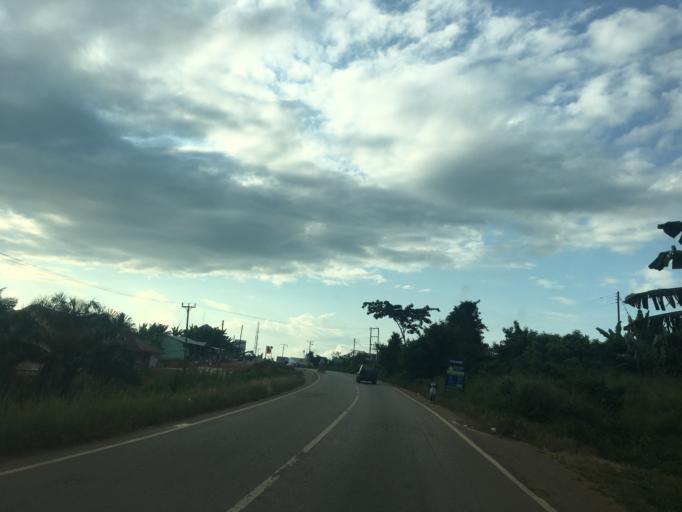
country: GH
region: Western
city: Bibiani
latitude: 6.4378
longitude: -2.3087
